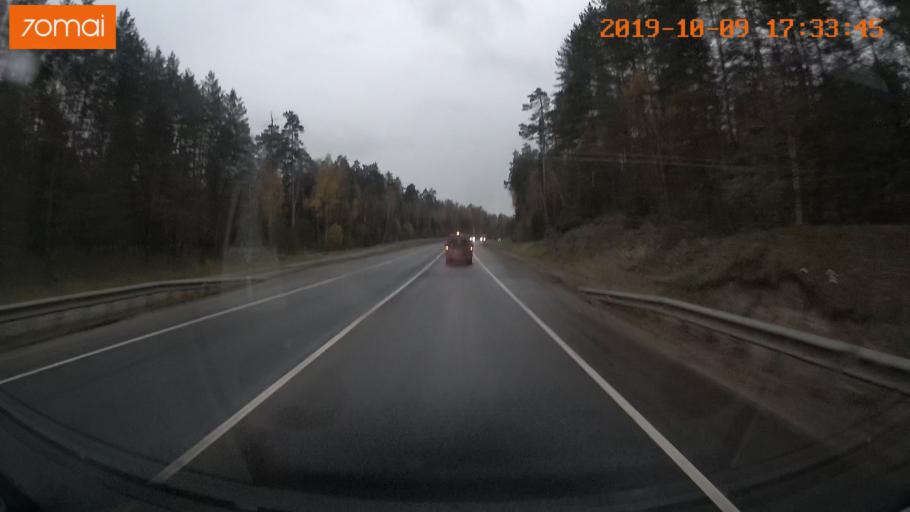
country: RU
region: Ivanovo
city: Bogorodskoye
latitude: 57.1140
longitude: 41.0178
